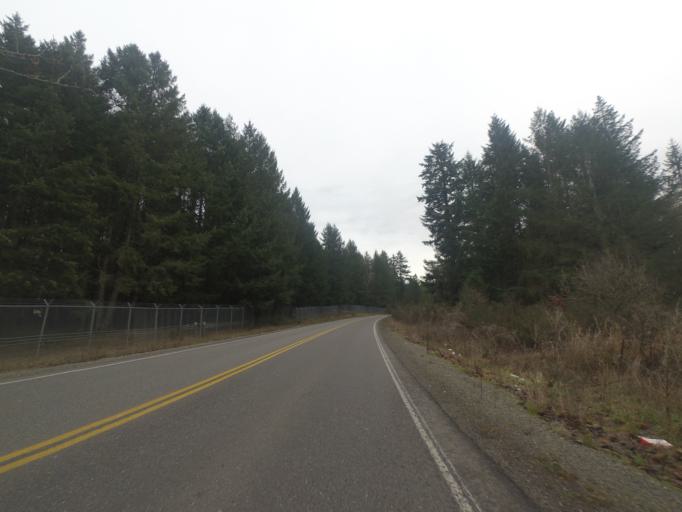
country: US
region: Washington
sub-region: Pierce County
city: McChord Air Force Base
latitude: 47.1208
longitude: -122.5084
